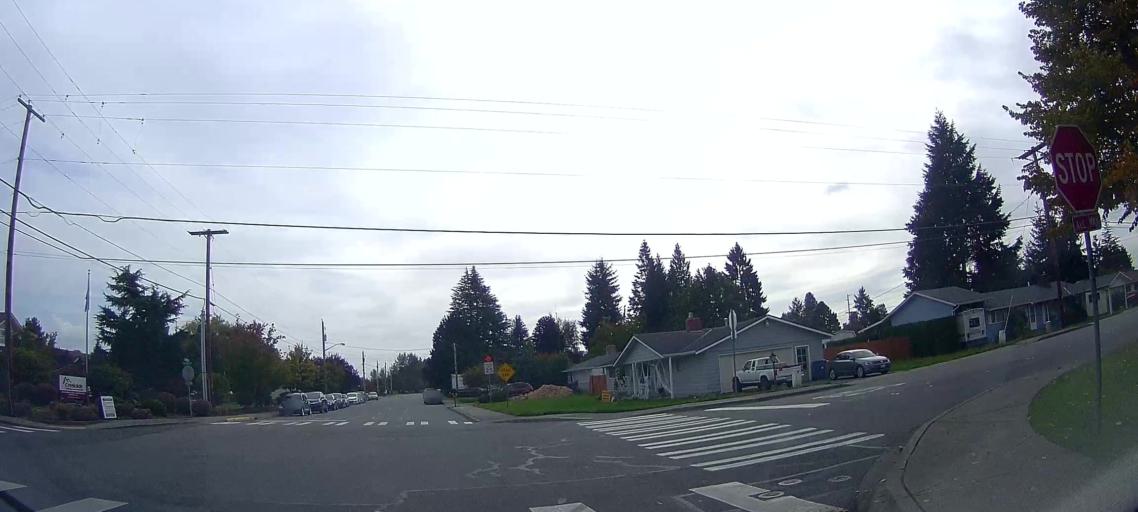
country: US
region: Washington
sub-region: Skagit County
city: Burlington
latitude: 48.4648
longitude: -122.3308
